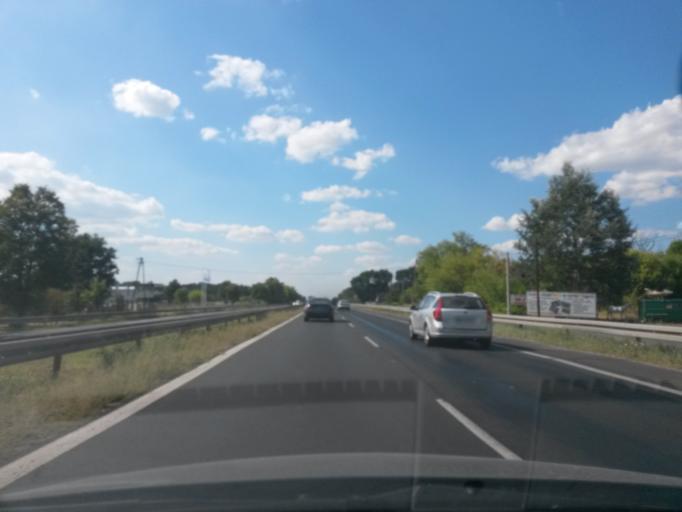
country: PL
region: Masovian Voivodeship
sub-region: Powiat warszawski zachodni
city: Dziekanow Lesny
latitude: 52.3611
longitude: 20.8245
